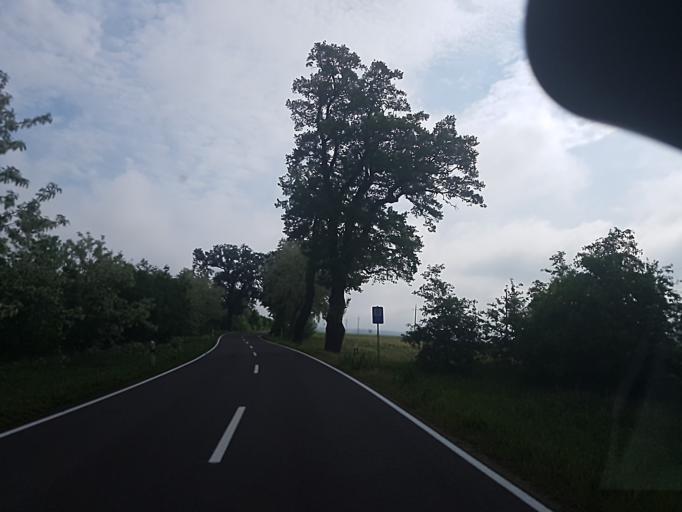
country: DE
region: Saxony-Anhalt
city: Lindau
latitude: 52.0301
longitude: 12.2389
